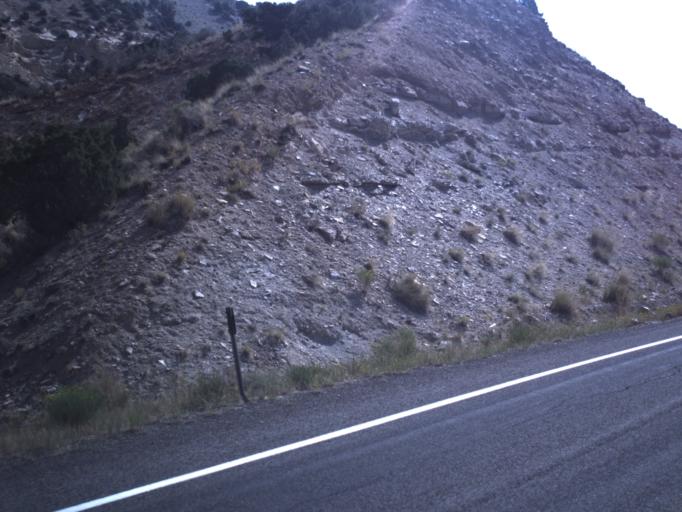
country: US
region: Utah
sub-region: Daggett County
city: Manila
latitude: 40.9334
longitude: -109.7160
